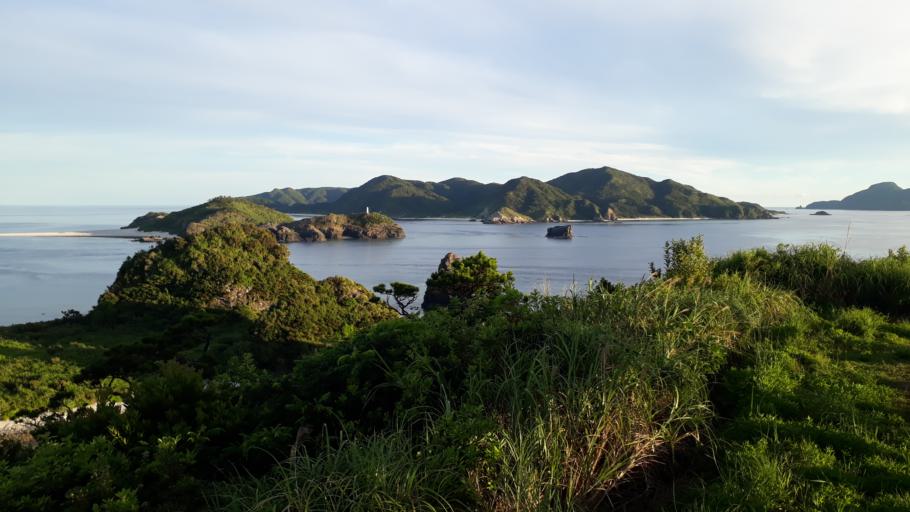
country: JP
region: Okinawa
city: Naha-shi
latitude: 26.2272
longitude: 127.2939
